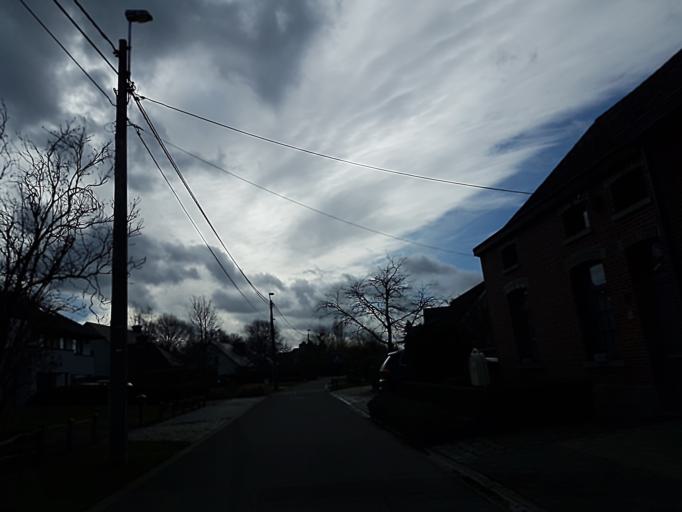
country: BE
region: Flanders
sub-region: Provincie Vlaams-Brabant
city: Zemst
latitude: 51.0063
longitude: 4.4325
